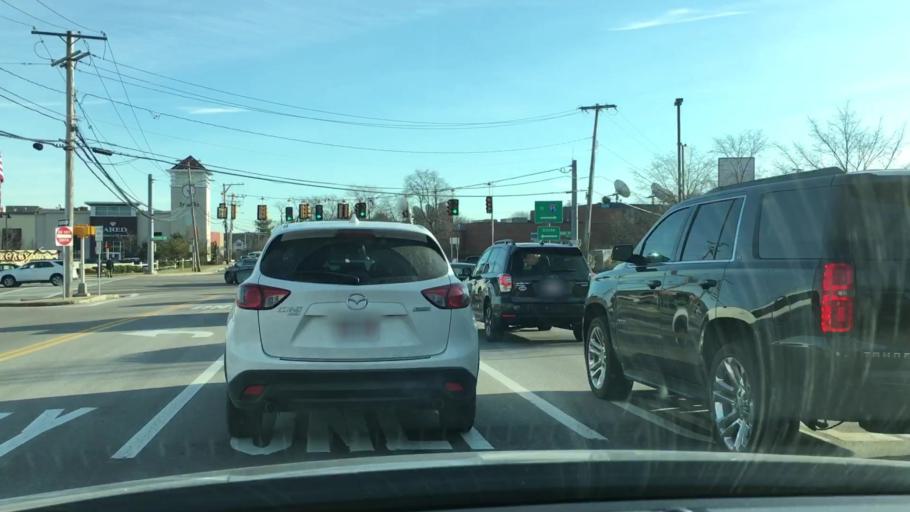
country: US
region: Massachusetts
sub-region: Norfolk County
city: Dedham
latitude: 42.2325
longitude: -71.1809
